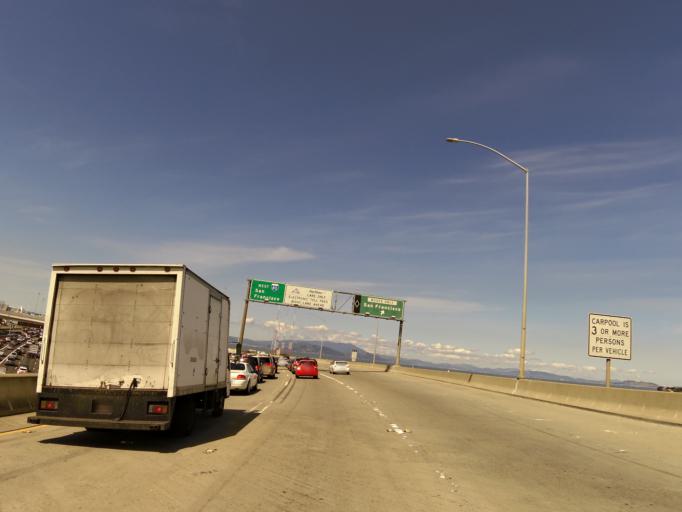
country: US
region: California
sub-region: Alameda County
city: Emeryville
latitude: 37.8253
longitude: -122.3060
